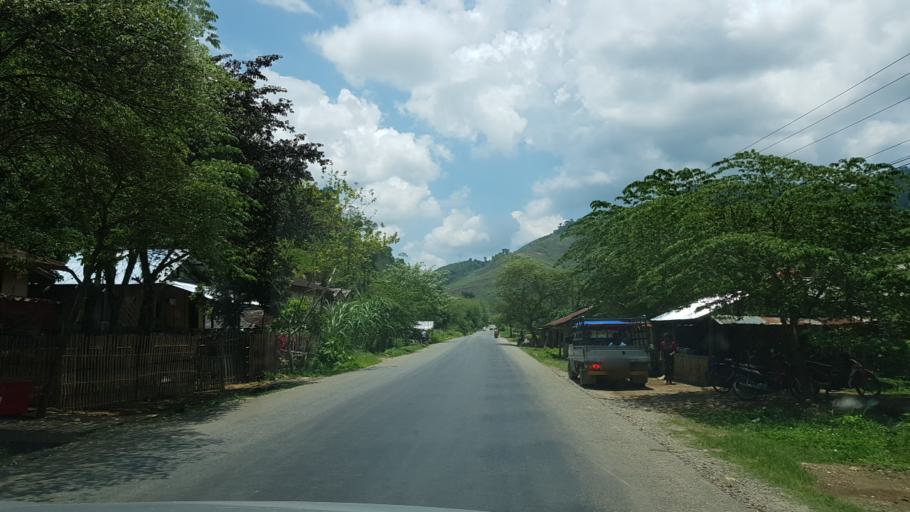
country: LA
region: Vientiane
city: Muang Kasi
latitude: 19.1313
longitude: 102.2767
